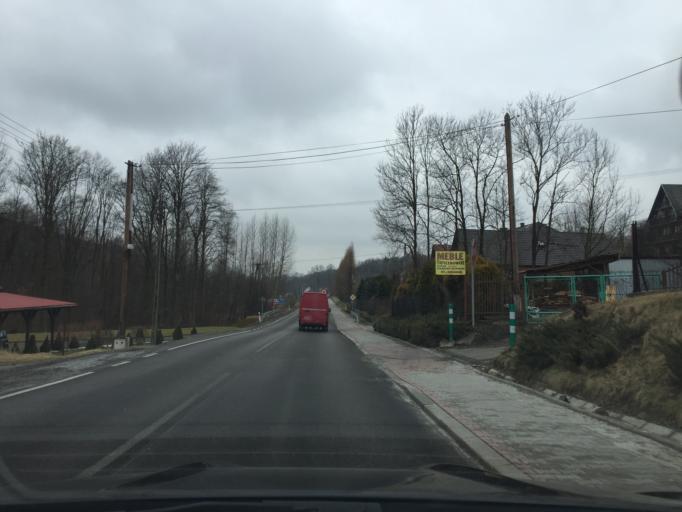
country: PL
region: Lesser Poland Voivodeship
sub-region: Powiat suski
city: Palcza
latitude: 49.8021
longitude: 19.7383
